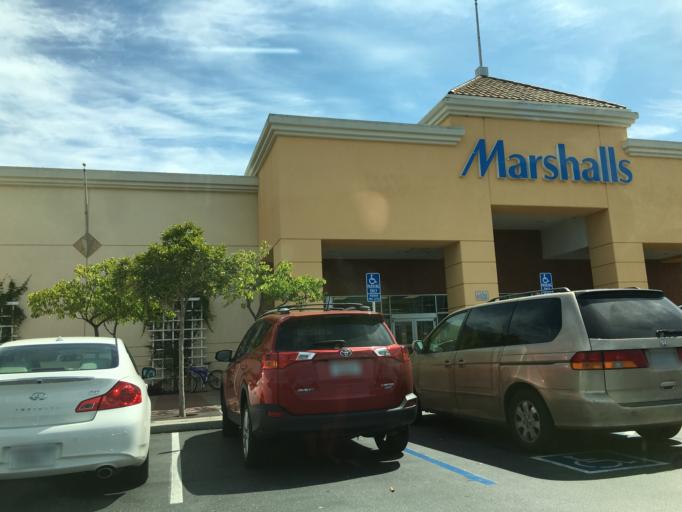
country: US
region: California
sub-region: San Mateo County
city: Foster City
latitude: 37.5597
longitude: -122.2821
